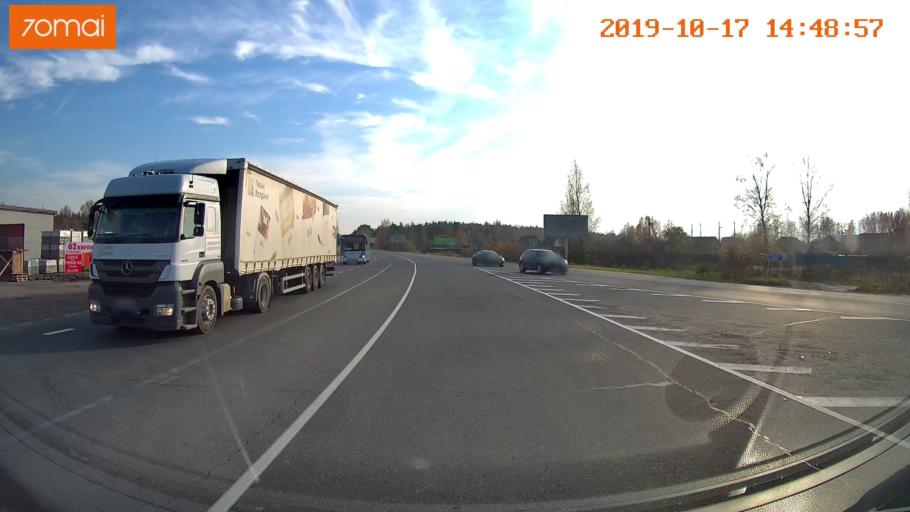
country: RU
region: Rjazan
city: Polyany
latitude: 54.7531
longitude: 39.8379
